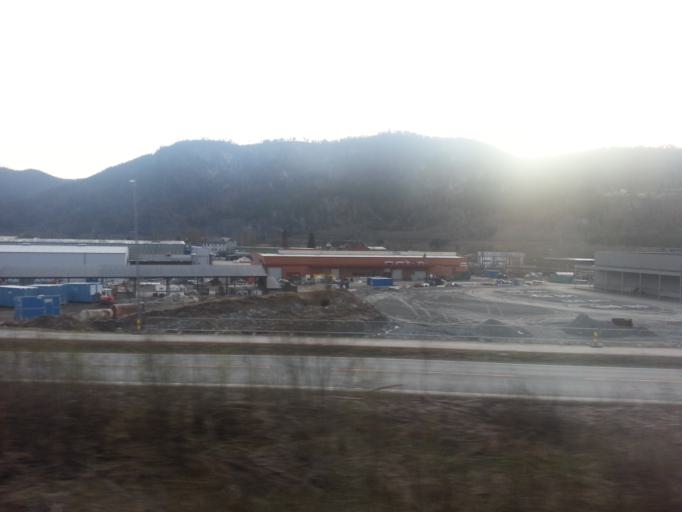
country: NO
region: Sor-Trondelag
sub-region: Midtre Gauldal
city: Storen
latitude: 63.0423
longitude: 10.2849
